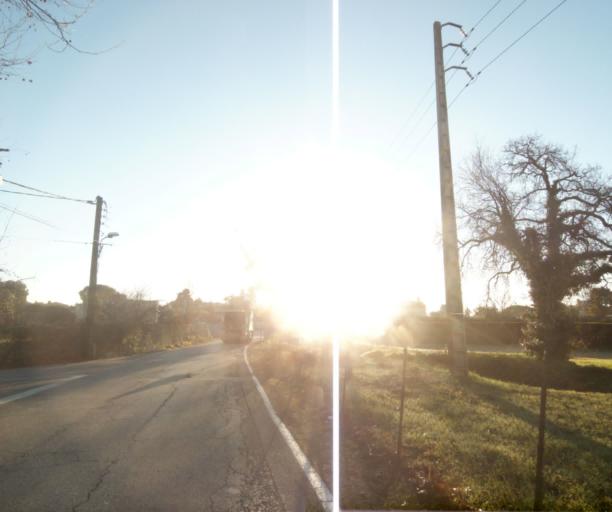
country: FR
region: Provence-Alpes-Cote d'Azur
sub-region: Departement des Alpes-Maritimes
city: Vallauris
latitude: 43.5753
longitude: 7.0823
